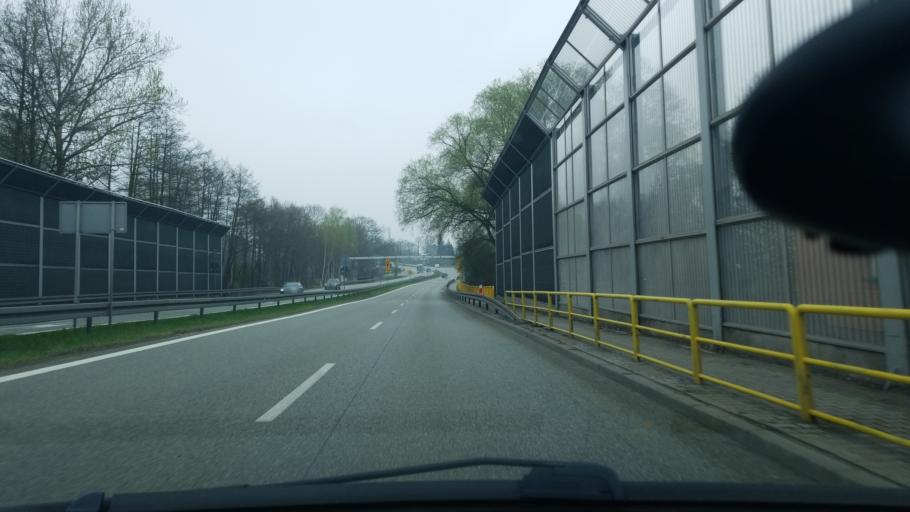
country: PL
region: Silesian Voivodeship
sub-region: Powiat pszczynski
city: Pawlowice
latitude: 49.9955
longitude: 18.7114
